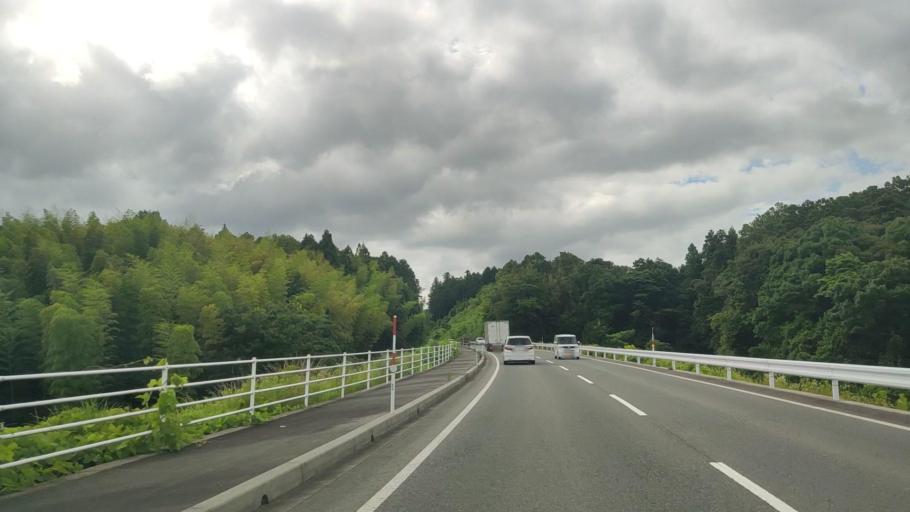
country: JP
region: Tottori
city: Yonago
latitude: 35.3801
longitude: 133.3891
